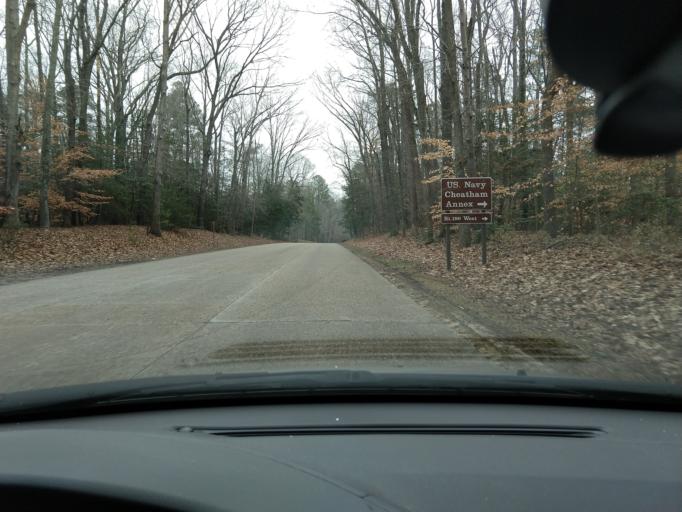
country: US
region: Virginia
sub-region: City of Williamsburg
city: Williamsburg
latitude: 37.2815
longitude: -76.6291
